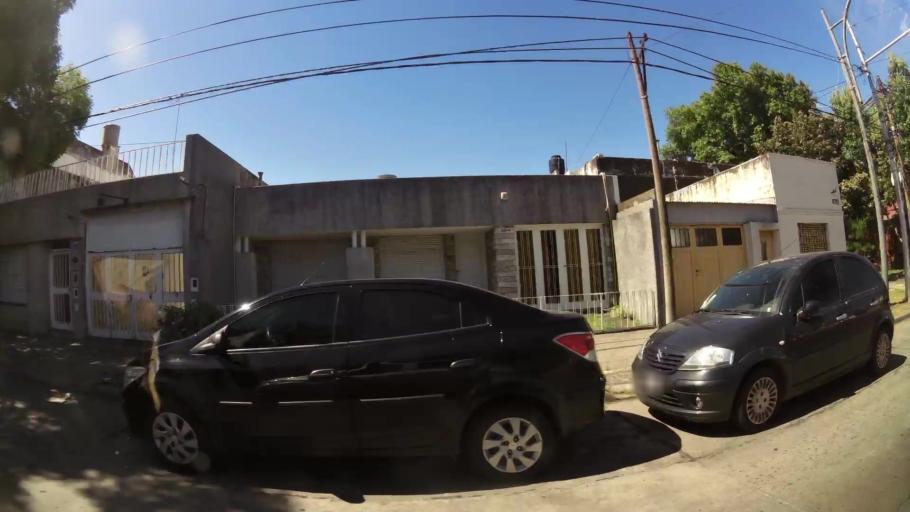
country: AR
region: Santa Fe
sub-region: Departamento de Rosario
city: Rosario
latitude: -32.9415
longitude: -60.6872
